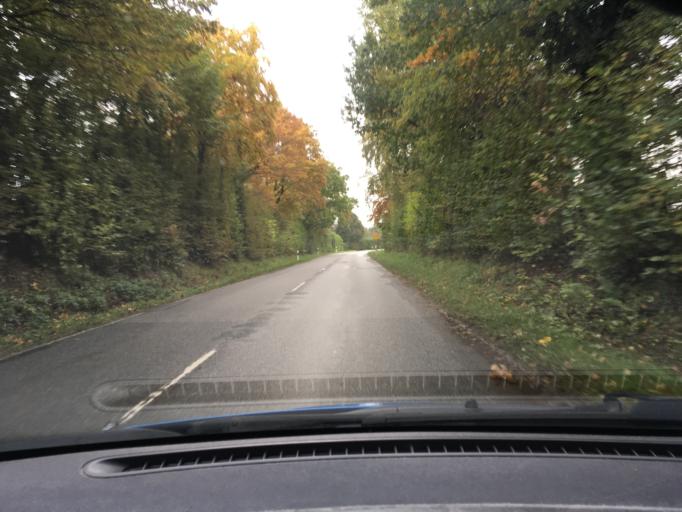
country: DE
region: Schleswig-Holstein
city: Klein Ronnau
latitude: 53.9761
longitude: 10.3096
